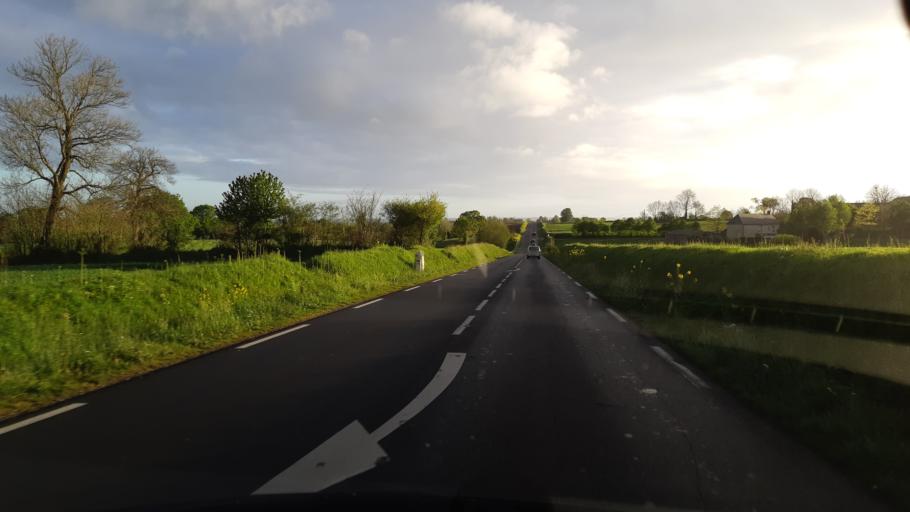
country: FR
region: Lower Normandy
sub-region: Departement de la Manche
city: Agneaux
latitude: 49.0342
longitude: -1.1347
